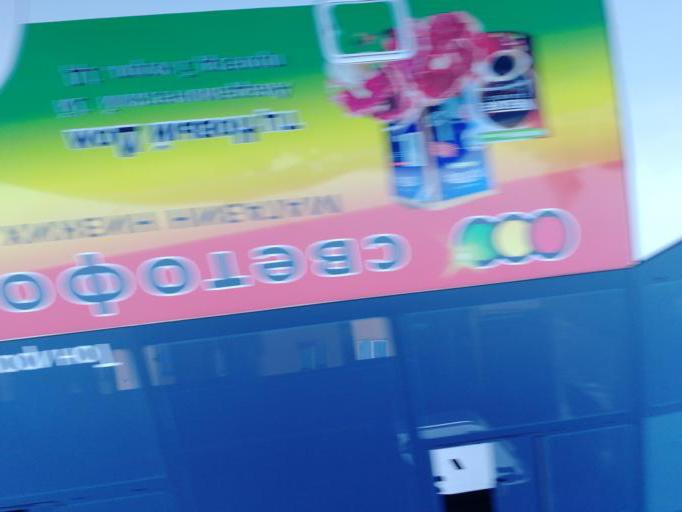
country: RU
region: Kaluga
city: Mstikhino
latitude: 54.4963
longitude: 36.1830
